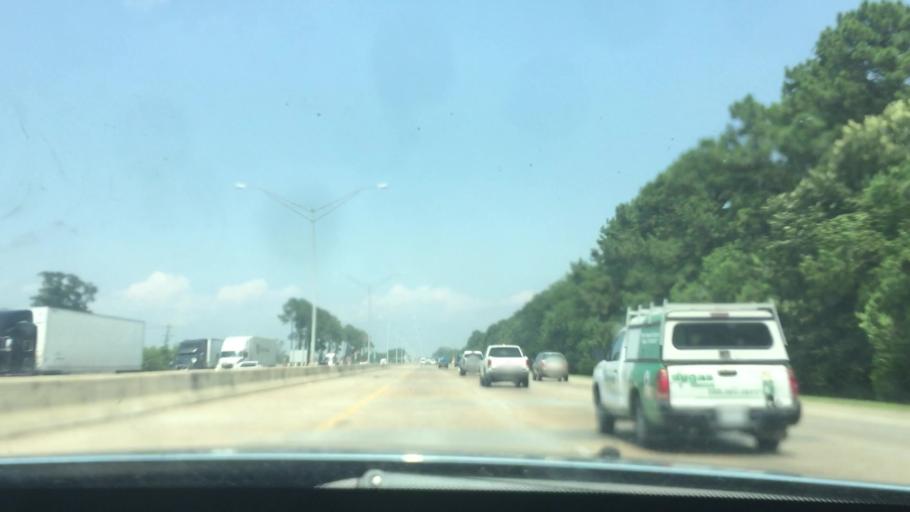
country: US
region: Louisiana
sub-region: East Baton Rouge Parish
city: Shenandoah
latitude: 30.4353
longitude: -91.0358
